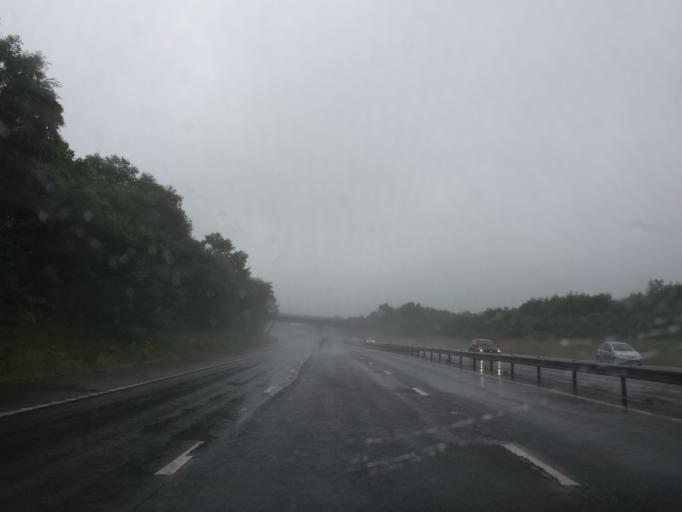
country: GB
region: England
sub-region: Leicestershire
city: Markfield
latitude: 52.7113
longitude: -1.2909
